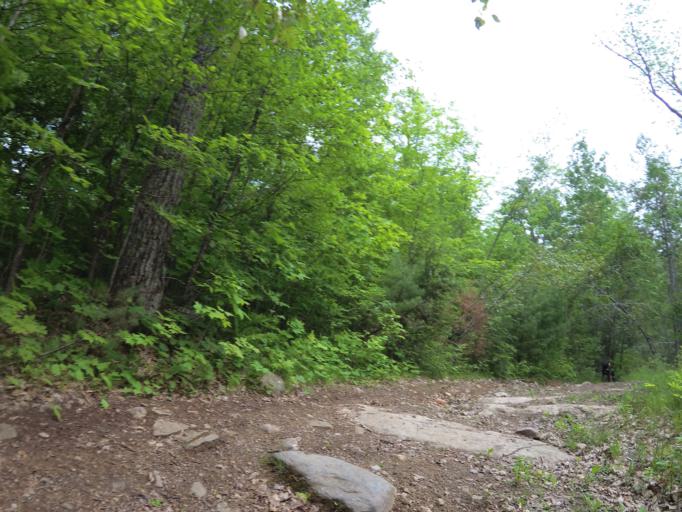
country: CA
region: Ontario
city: Renfrew
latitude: 45.0634
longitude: -76.8914
